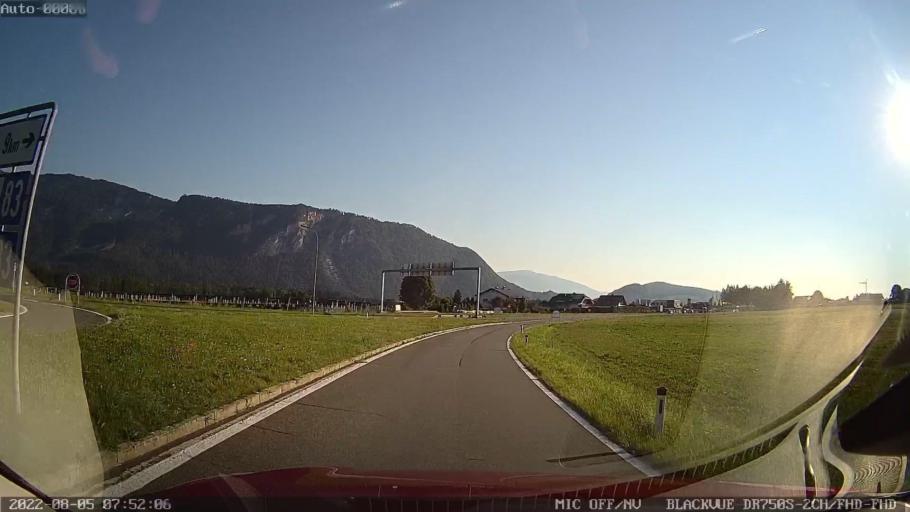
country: AT
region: Carinthia
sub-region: Politischer Bezirk Villach Land
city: Finkenstein am Faaker See
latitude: 46.5558
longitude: 13.7885
